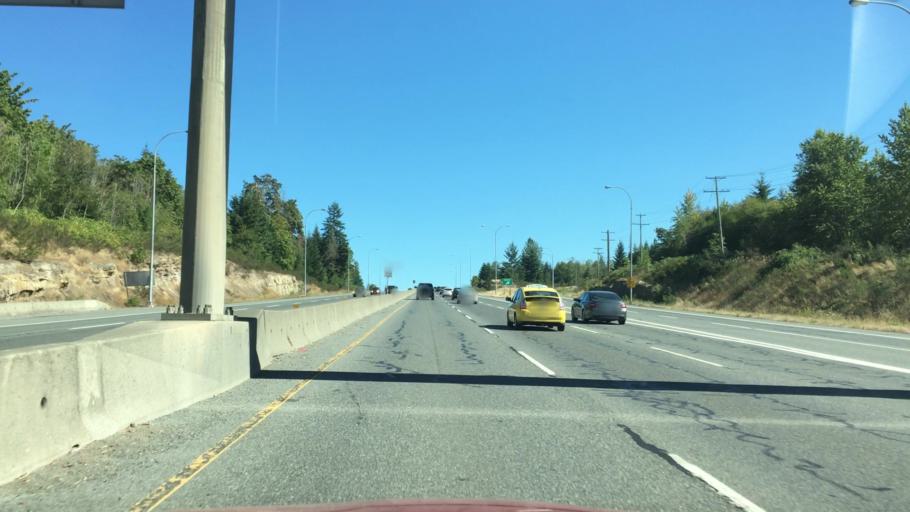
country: CA
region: British Columbia
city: Nanaimo
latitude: 49.1157
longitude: -123.9086
